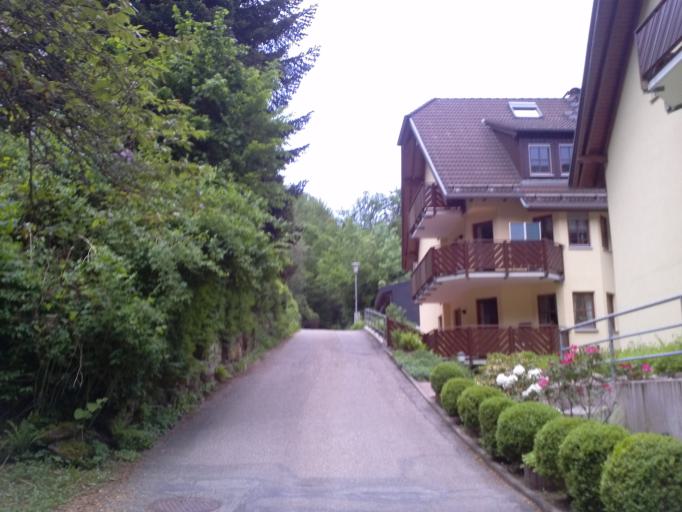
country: DE
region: Baden-Wuerttemberg
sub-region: Karlsruhe Region
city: Bad Herrenalb
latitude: 48.8041
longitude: 8.4397
